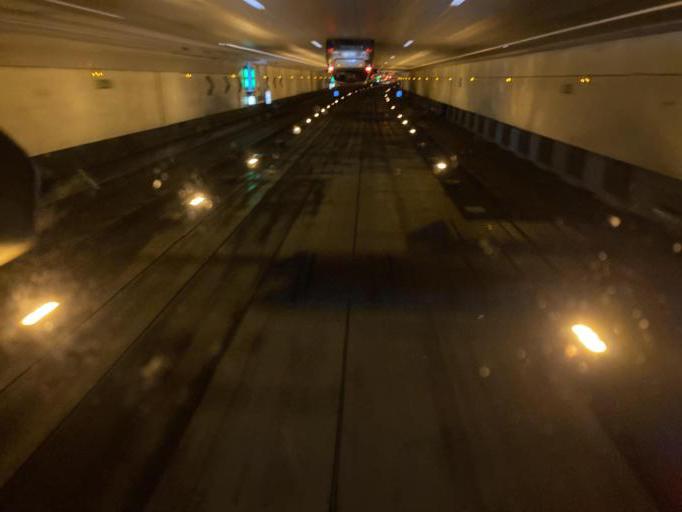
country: FR
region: Ile-de-France
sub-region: Departement des Hauts-de-Seine
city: Boulogne-Billancourt
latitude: 48.8485
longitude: 2.2404
